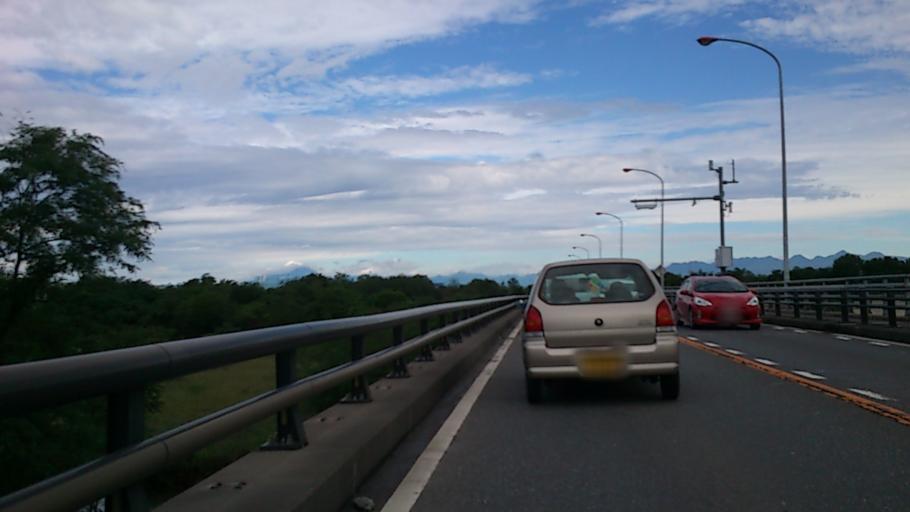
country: JP
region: Gunma
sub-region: Sawa-gun
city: Tamamura
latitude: 36.2669
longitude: 139.1224
